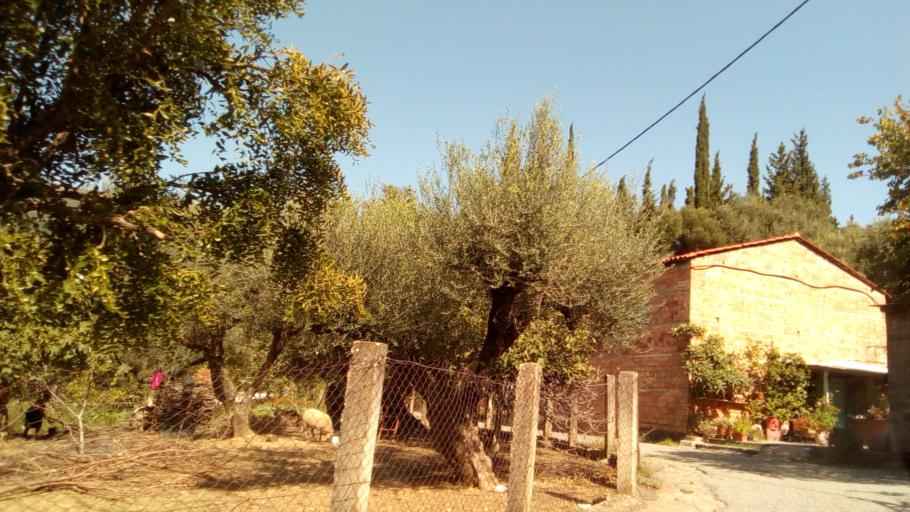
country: GR
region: West Greece
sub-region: Nomos Aitolias kai Akarnanias
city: Nafpaktos
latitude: 38.3925
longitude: 21.8114
